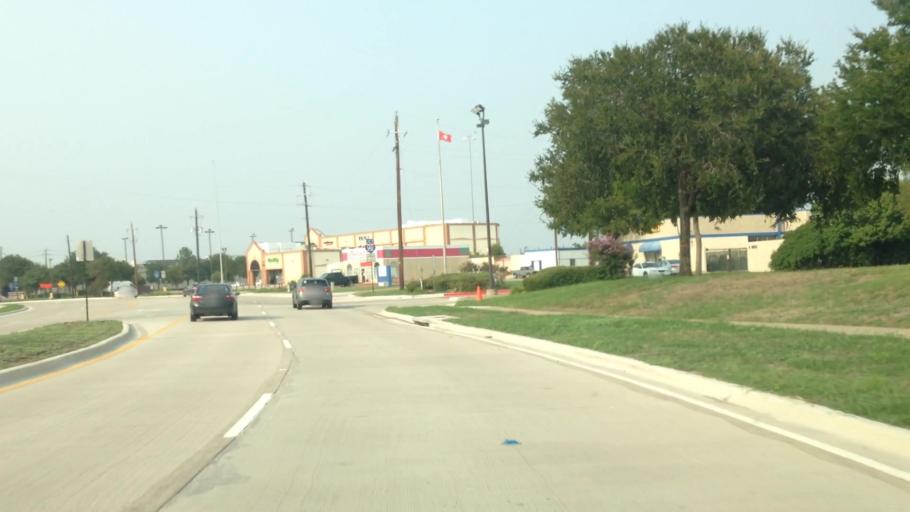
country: US
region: Texas
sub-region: Dallas County
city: Carrollton
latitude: 32.9805
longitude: -96.9208
